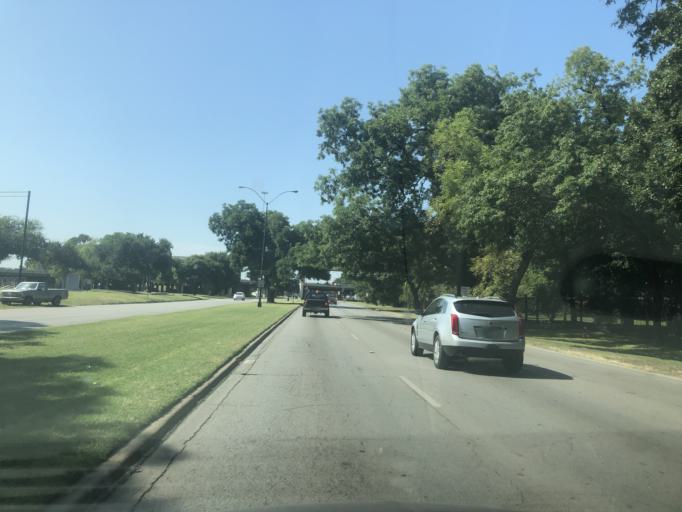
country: US
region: Texas
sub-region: Tarrant County
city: Fort Worth
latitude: 32.7360
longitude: -97.3614
